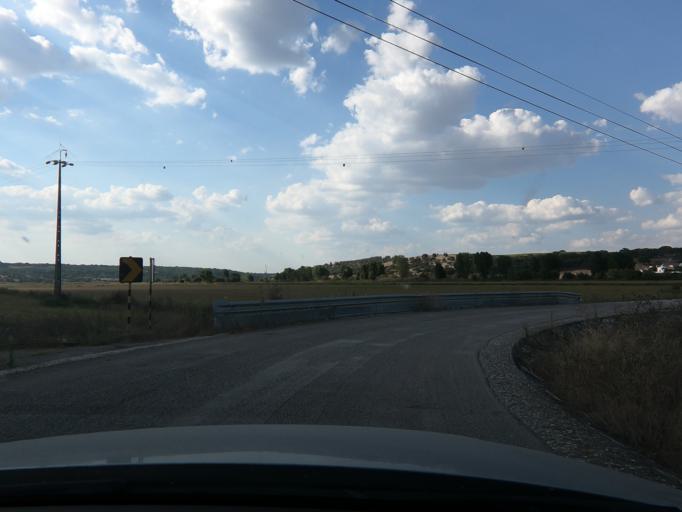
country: PT
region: Setubal
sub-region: Alcacer do Sal
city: Alcacer do Sal
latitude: 38.2487
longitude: -8.3589
